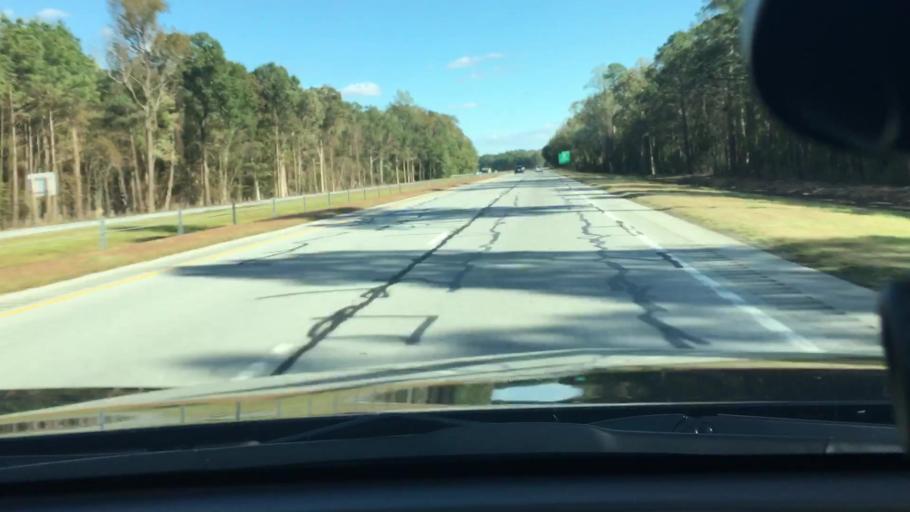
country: US
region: North Carolina
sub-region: Pitt County
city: Farmville
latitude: 35.6154
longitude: -77.6293
